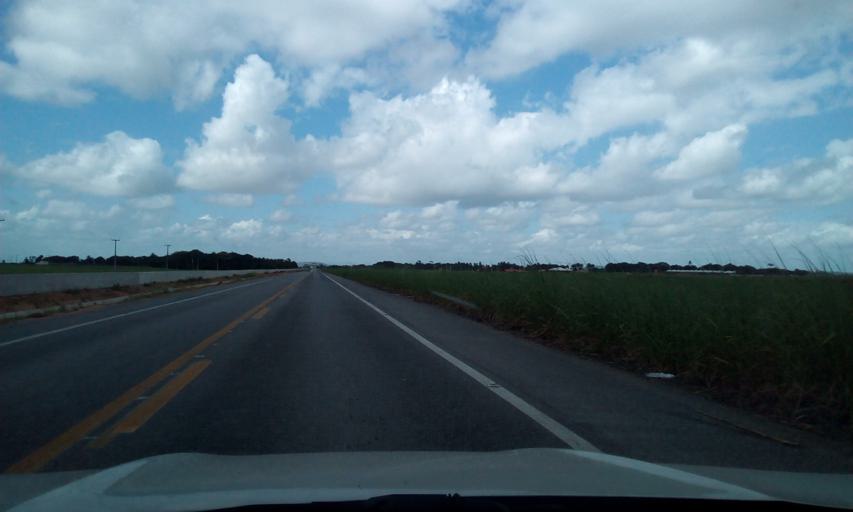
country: BR
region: Alagoas
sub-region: Pilar
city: Pilar
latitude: -9.5805
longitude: -35.9731
